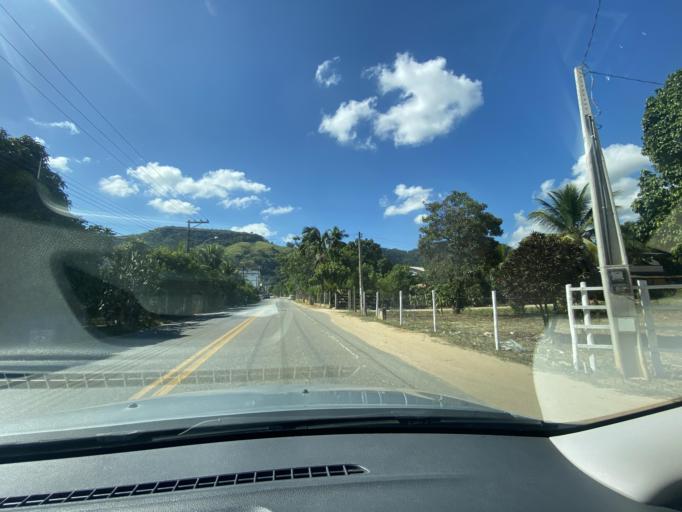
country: BR
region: Espirito Santo
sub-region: Jeronimo Monteiro
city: Jeronimo Monteiro
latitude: -20.7946
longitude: -41.4062
